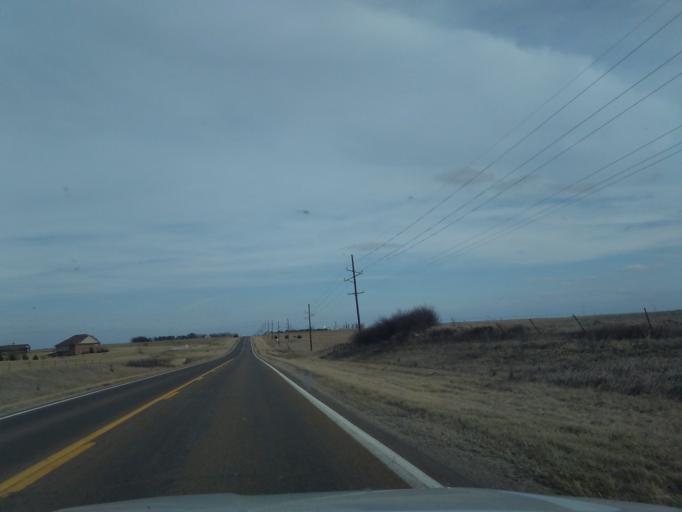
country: US
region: Nebraska
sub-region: Saline County
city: Wilber
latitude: 40.3061
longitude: -97.0249
